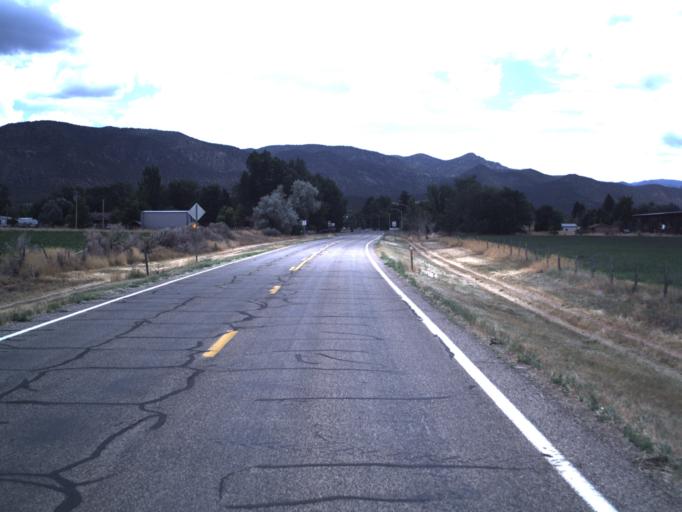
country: US
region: Utah
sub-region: Iron County
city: Parowan
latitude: 37.8921
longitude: -112.7749
